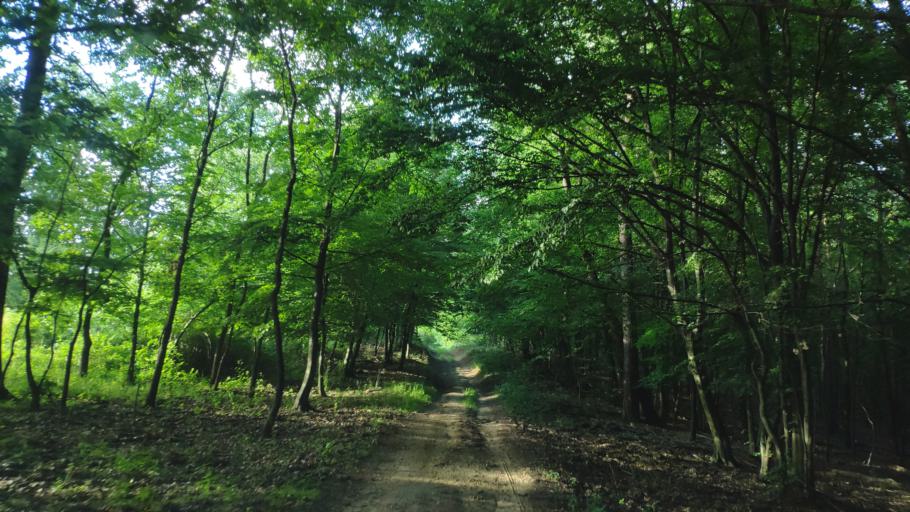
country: HU
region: Borsod-Abauj-Zemplen
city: Arlo
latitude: 48.2410
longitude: 20.1390
